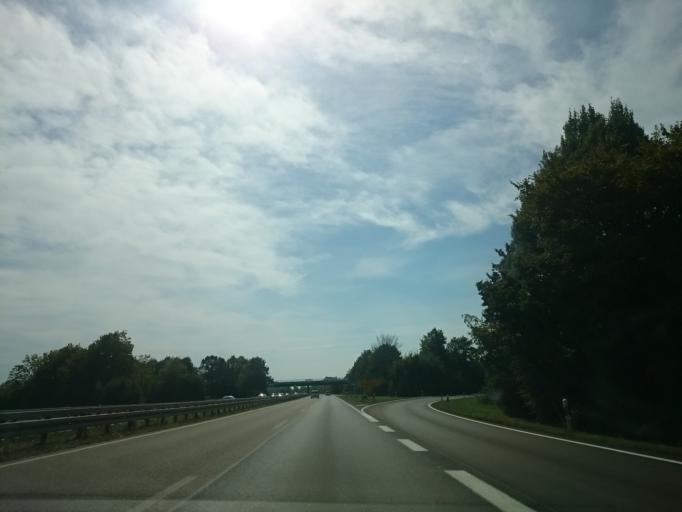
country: DE
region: Bavaria
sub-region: Swabia
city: Asbach-Baumenheim
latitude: 48.7049
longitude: 10.8054
